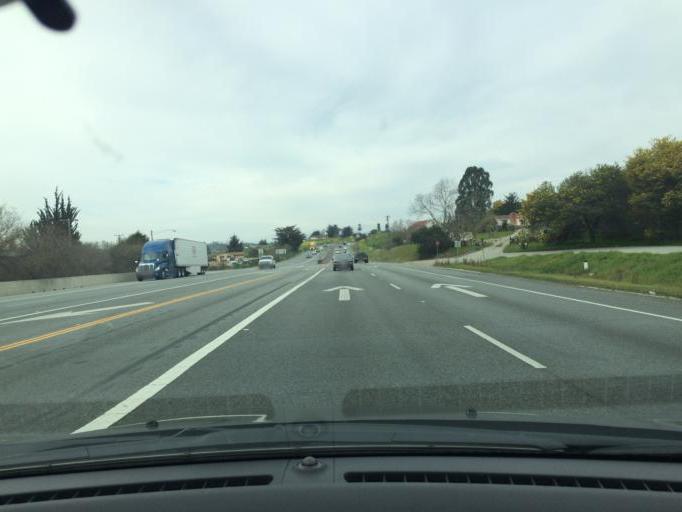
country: US
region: California
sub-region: San Benito County
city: Aromas
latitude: 36.8443
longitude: -121.6342
